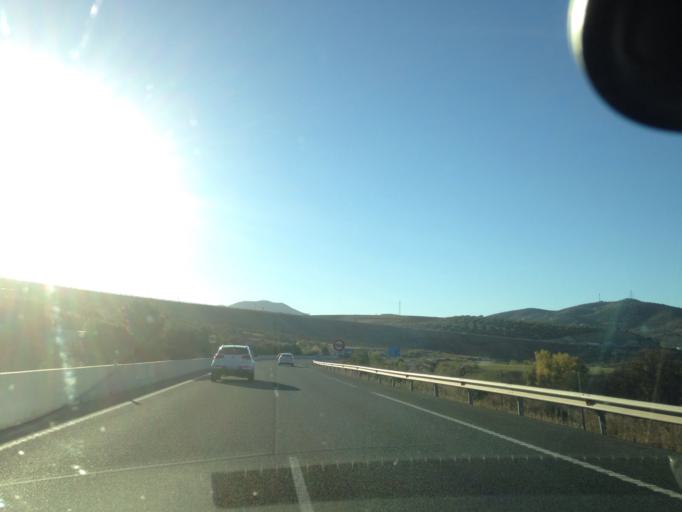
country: ES
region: Andalusia
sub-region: Provincia de Malaga
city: Casabermeja
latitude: 36.9165
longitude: -4.4447
